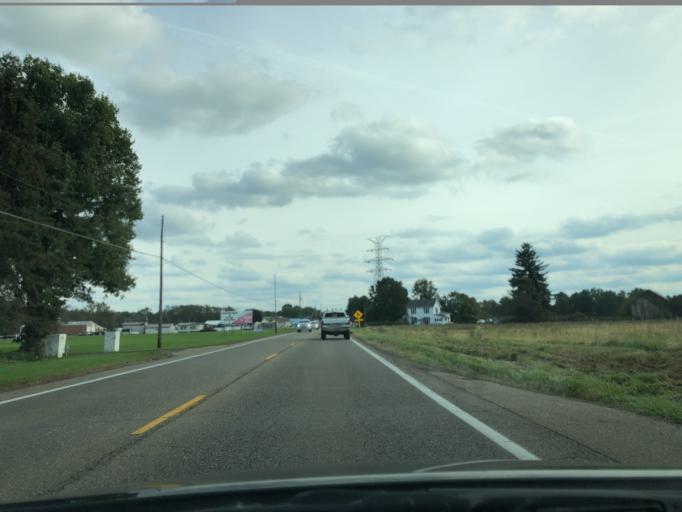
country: US
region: Ohio
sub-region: Tuscarawas County
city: Strasburg
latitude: 40.6194
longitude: -81.5416
